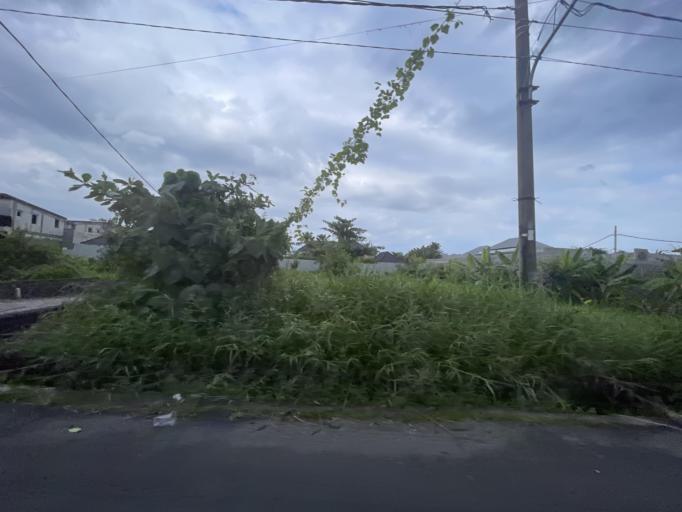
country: ID
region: Bali
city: Banjar Gunungpande
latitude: -8.6663
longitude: 115.1445
